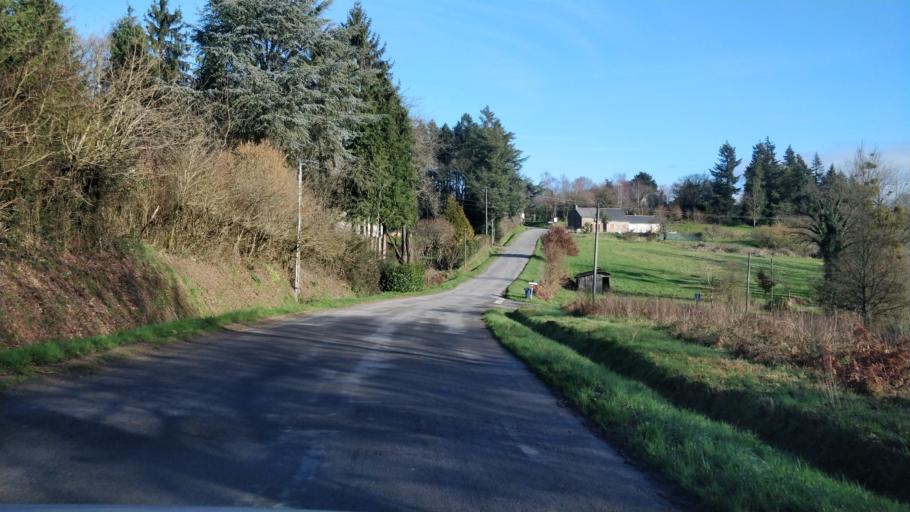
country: FR
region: Brittany
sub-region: Departement d'Ille-et-Vilaine
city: Sens-de-Bretagne
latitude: 48.3476
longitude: -1.4894
